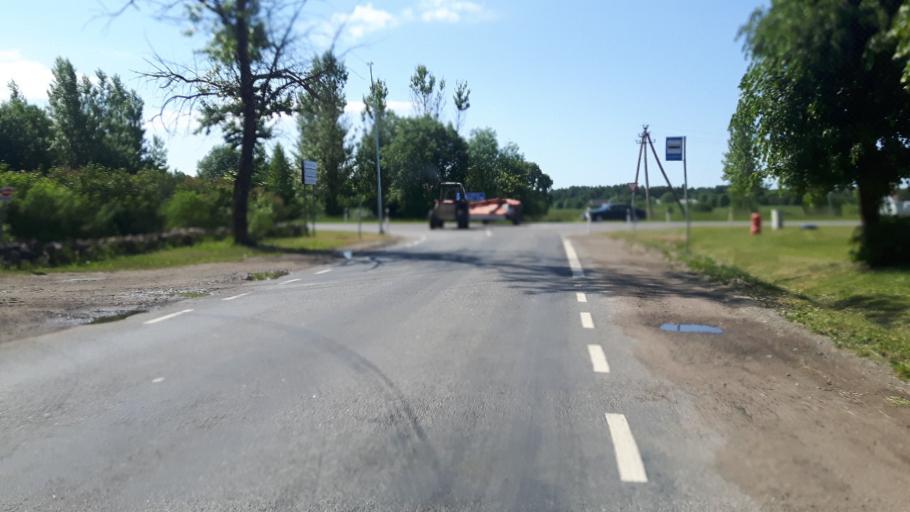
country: EE
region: Paernumaa
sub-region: Vaendra vald (alev)
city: Vandra
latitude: 58.6520
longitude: 25.0226
